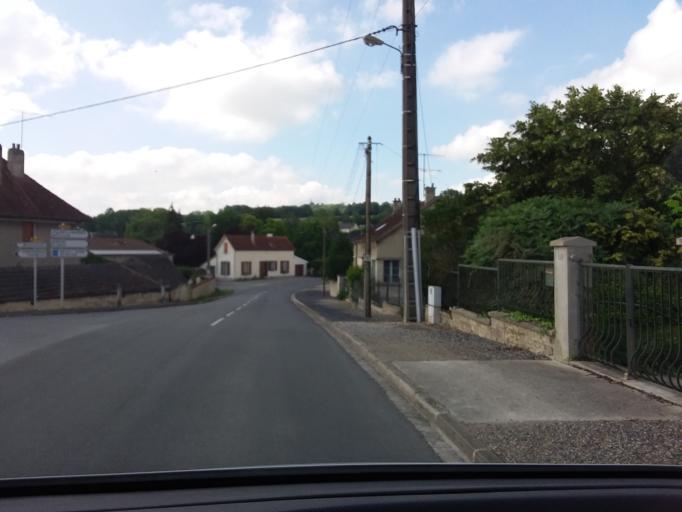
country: FR
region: Champagne-Ardenne
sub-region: Departement de la Marne
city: Fismes
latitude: 49.3798
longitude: 3.7306
